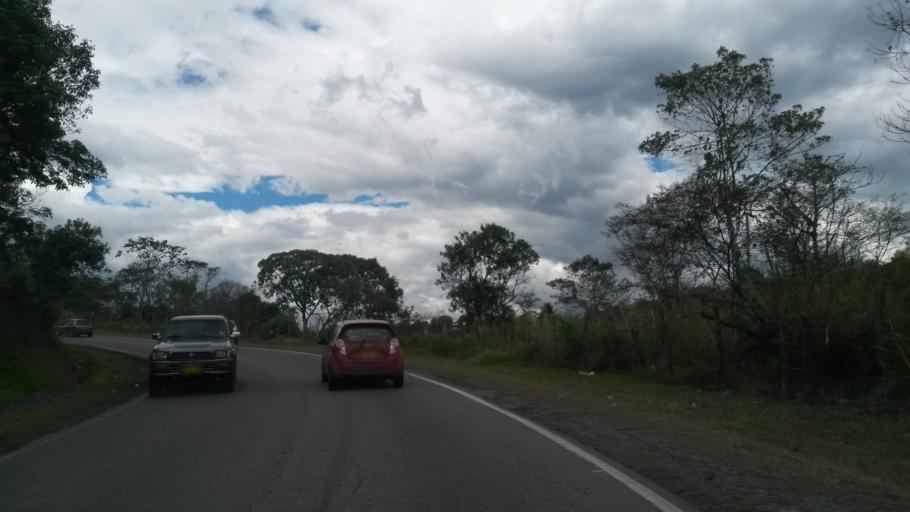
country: CO
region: Cauca
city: Rosas
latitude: 2.3408
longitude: -76.6925
